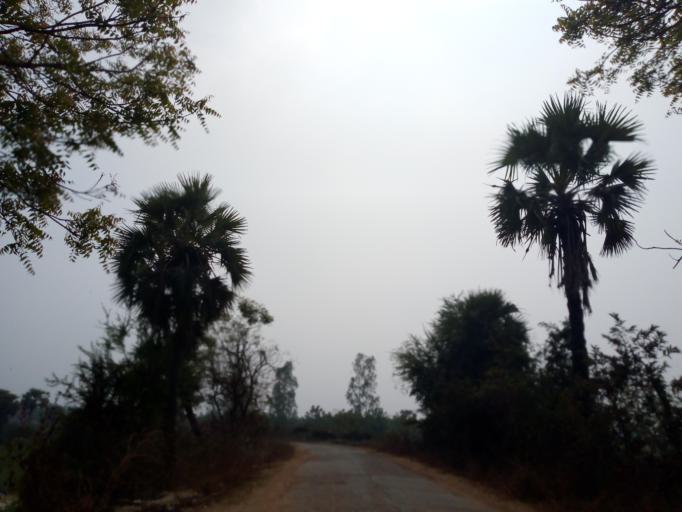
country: IN
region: Andhra Pradesh
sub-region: West Godavari
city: Tadepallegudem
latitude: 16.8699
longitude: 81.3196
